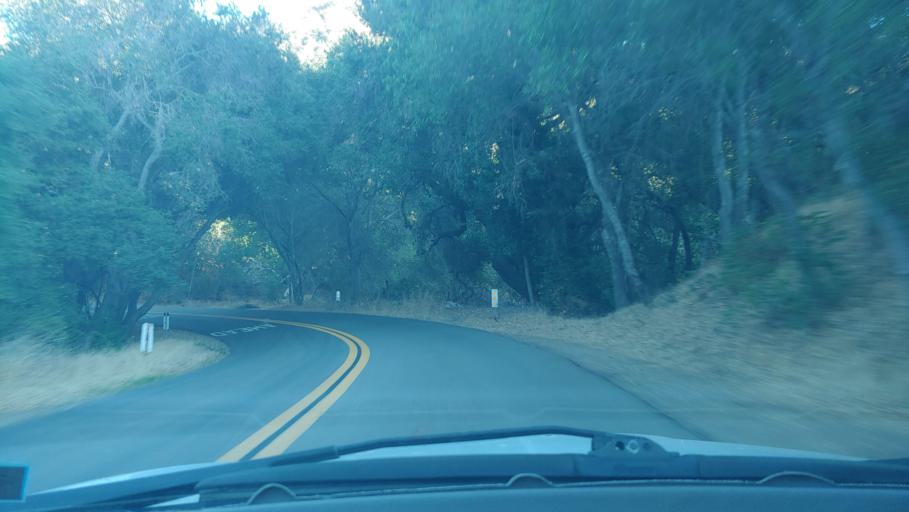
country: US
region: California
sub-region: Santa Barbara County
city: Goleta
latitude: 34.5352
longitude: -119.8512
